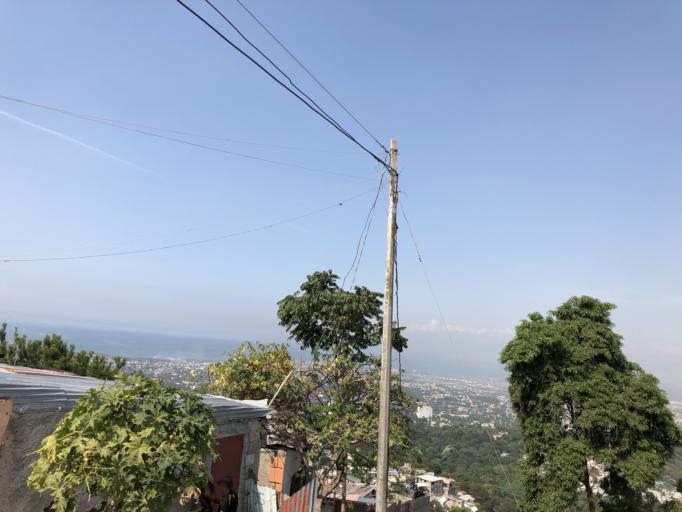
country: HT
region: Ouest
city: Port-au-Prince
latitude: 18.5213
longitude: -72.3157
